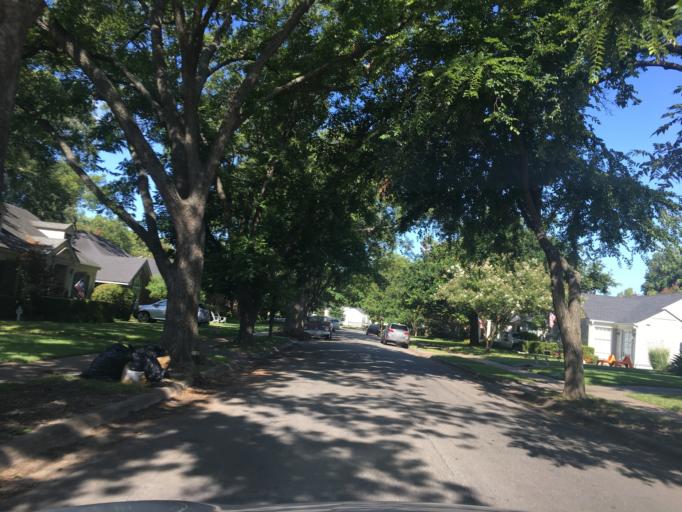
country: US
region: Texas
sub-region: Dallas County
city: Highland Park
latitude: 32.8349
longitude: -96.7628
